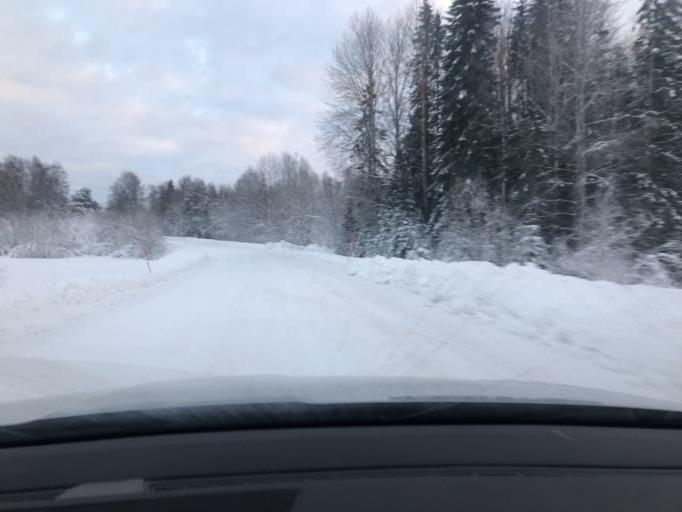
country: SE
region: Vaesternorrland
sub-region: Kramfors Kommun
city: Nordingra
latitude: 63.0058
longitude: 18.1965
